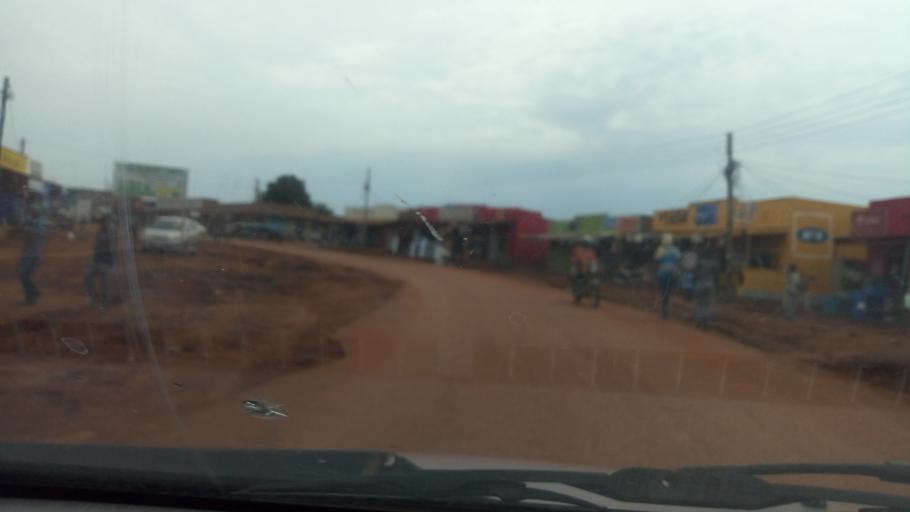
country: UG
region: Western Region
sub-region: Kiryandongo District
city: Kiryandongo
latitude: 1.8103
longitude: 32.0099
